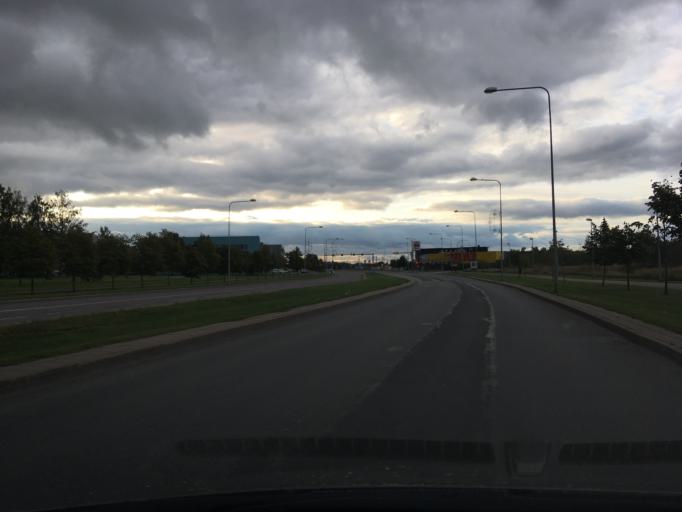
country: EE
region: Harju
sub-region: Tallinna linn
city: Kose
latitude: 59.4401
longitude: 24.8682
